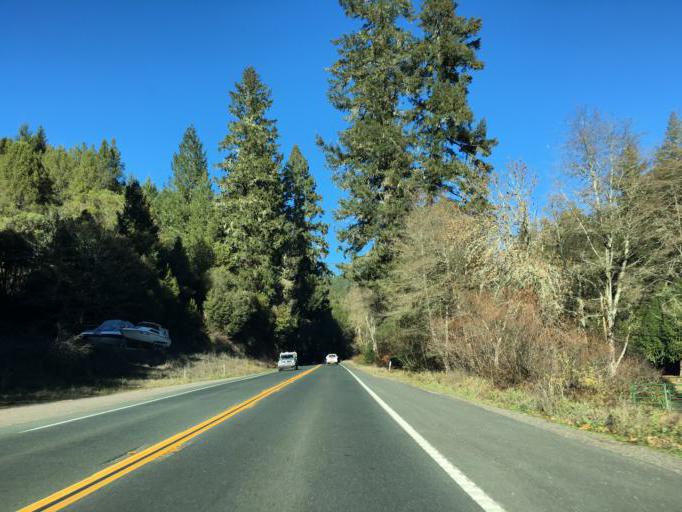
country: US
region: California
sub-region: Mendocino County
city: Brooktrails
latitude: 39.4833
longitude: -123.3612
